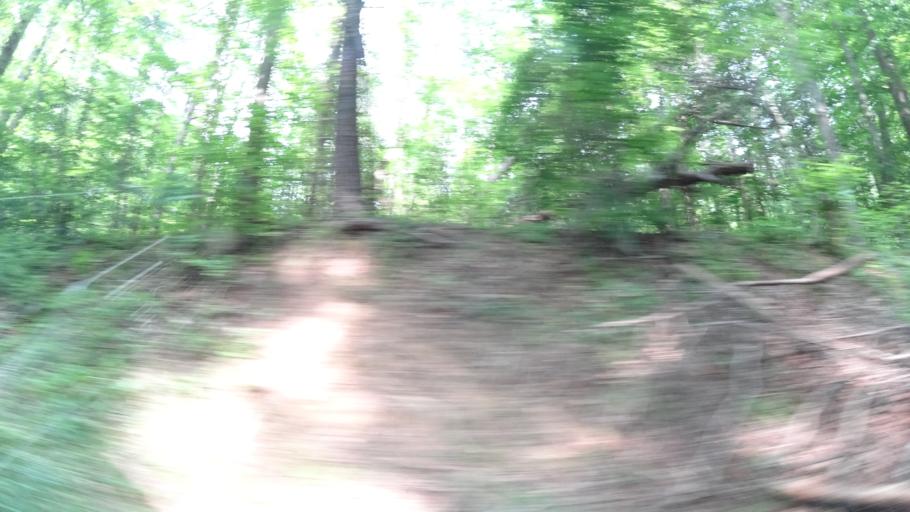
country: US
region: Virginia
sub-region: Spotsylvania County
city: Spotsylvania Courthouse
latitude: 38.1578
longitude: -77.6354
